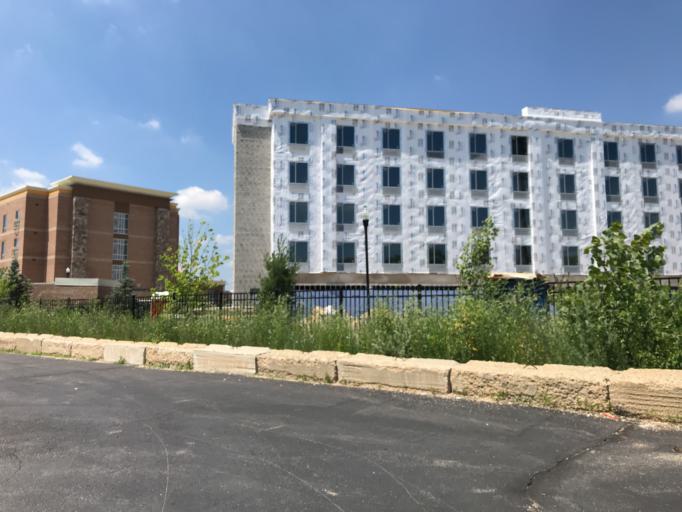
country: US
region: Michigan
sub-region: Oakland County
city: West Bloomfield Township
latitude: 42.5304
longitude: -83.3579
